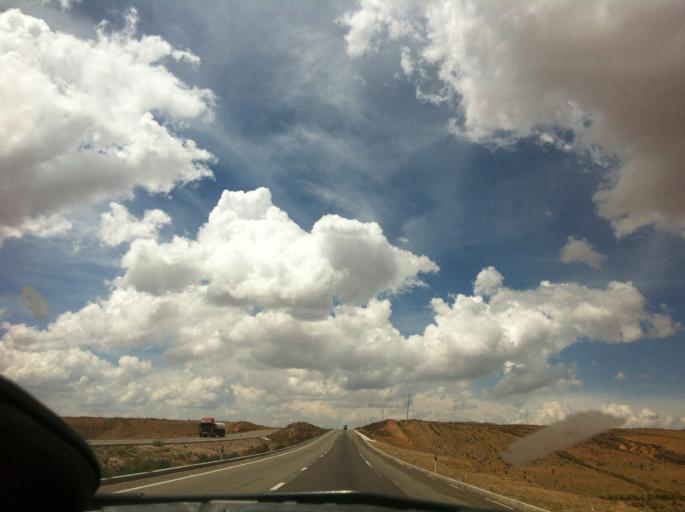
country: BO
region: La Paz
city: La Paz
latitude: -16.8918
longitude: -68.1267
